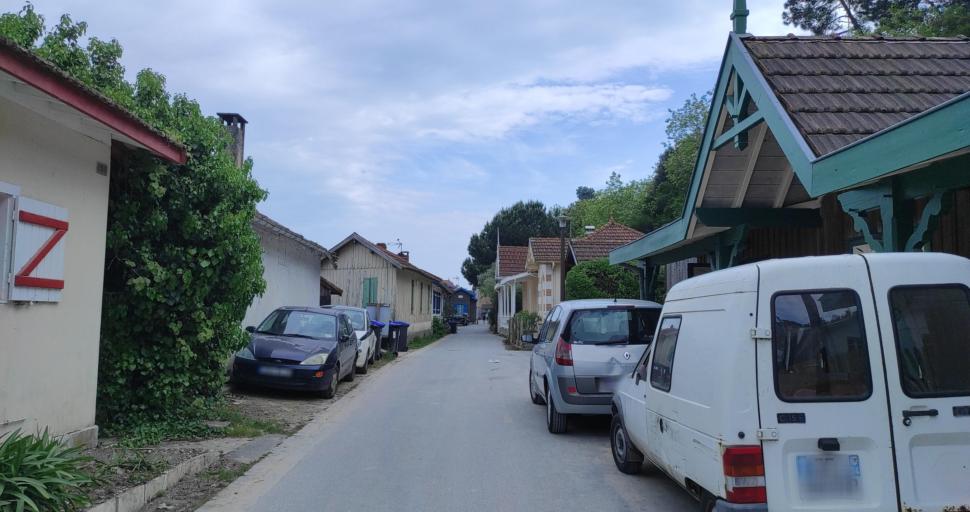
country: FR
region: Aquitaine
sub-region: Departement de la Gironde
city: Arcachon
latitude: 44.6923
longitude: -1.2330
